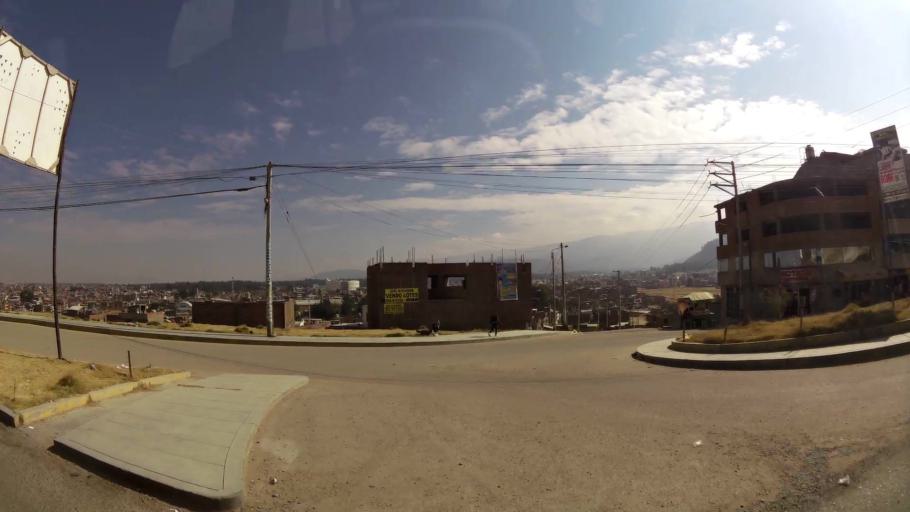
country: PE
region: Junin
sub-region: Provincia de Huancayo
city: Huancayo
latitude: -12.0578
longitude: -75.1935
